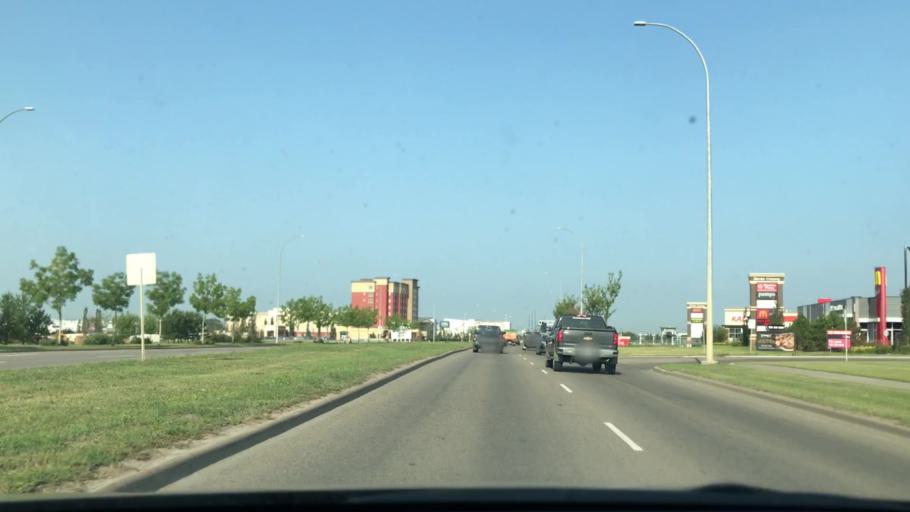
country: CA
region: Alberta
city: Beaumont
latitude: 53.4251
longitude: -113.4814
